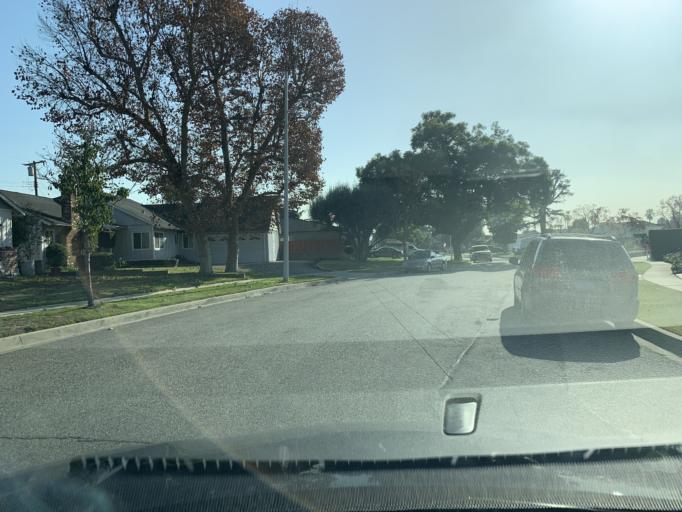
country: US
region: California
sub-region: Los Angeles County
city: Covina
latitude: 34.0816
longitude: -117.8961
